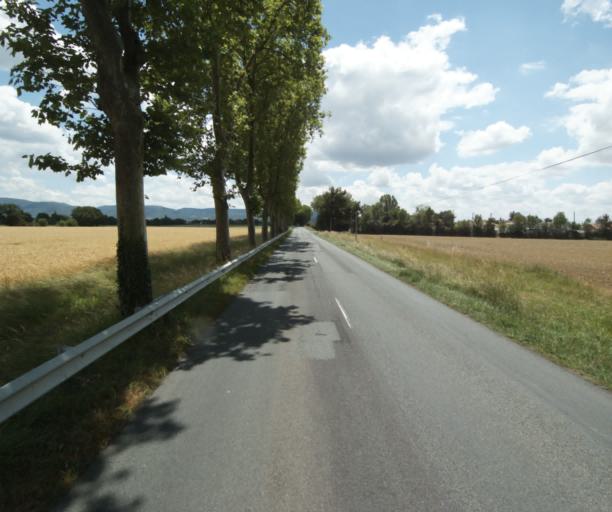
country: FR
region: Midi-Pyrenees
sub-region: Departement de la Haute-Garonne
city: Revel
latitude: 43.4981
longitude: 2.0123
